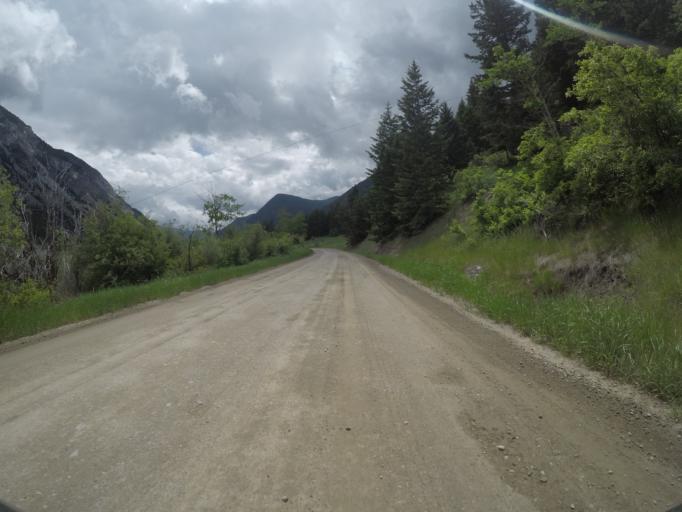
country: US
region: Montana
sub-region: Park County
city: Livingston
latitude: 45.5104
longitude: -110.2273
